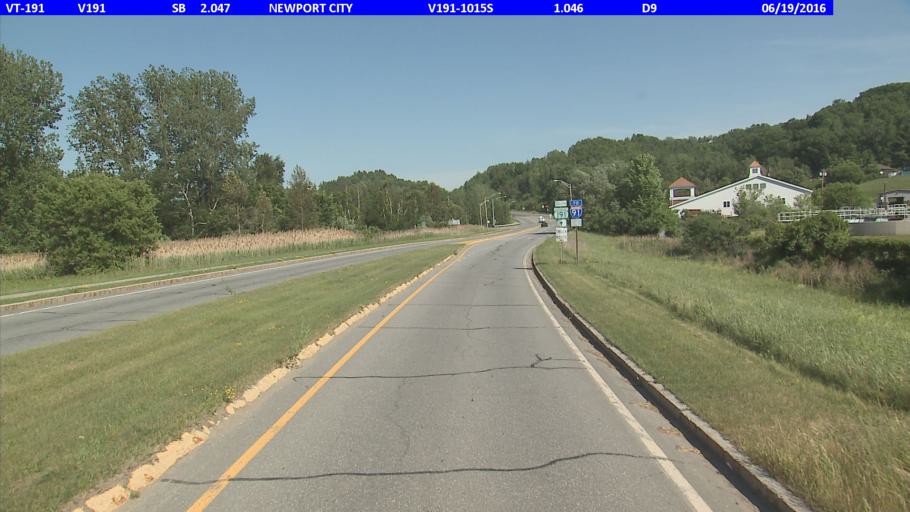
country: US
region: Vermont
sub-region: Orleans County
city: Newport
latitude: 44.9406
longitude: -72.1994
